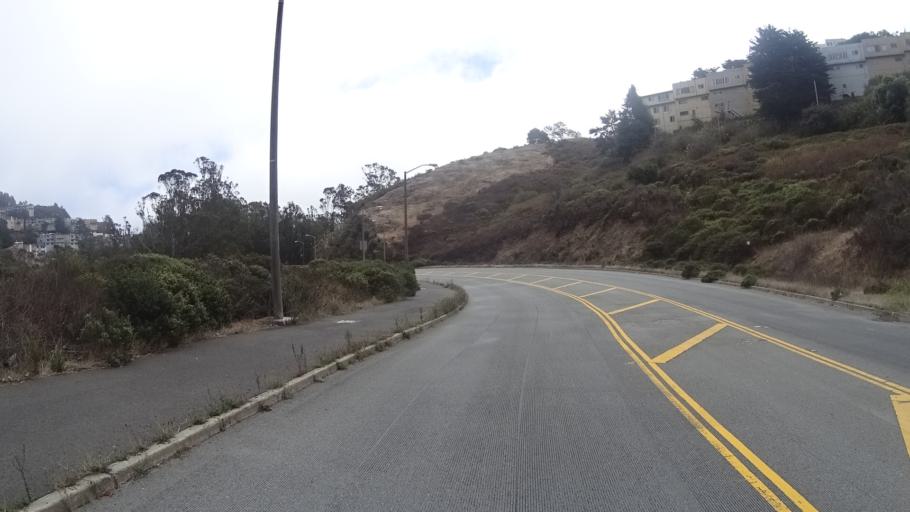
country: US
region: California
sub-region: San Mateo County
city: Daly City
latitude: 37.7405
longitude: -122.4442
